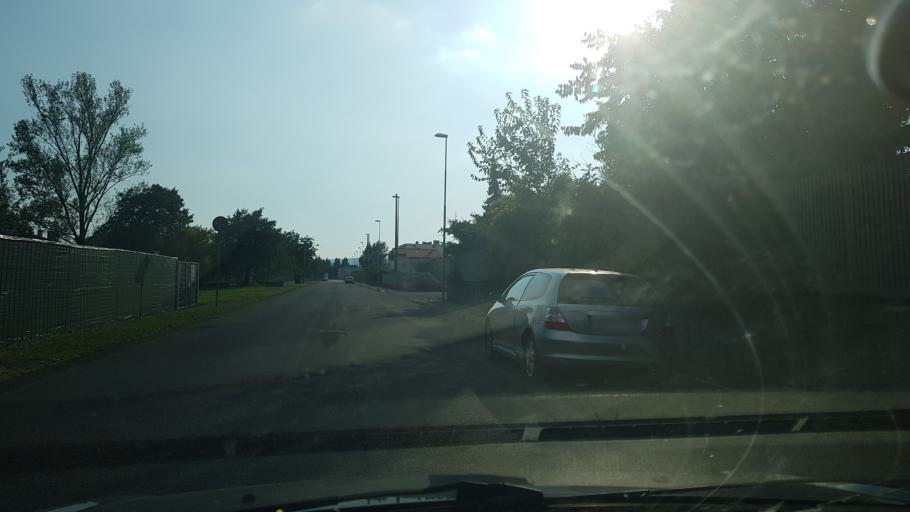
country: IT
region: Friuli Venezia Giulia
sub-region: Provincia di Gorizia
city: Gorizia
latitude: 45.9260
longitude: 13.6210
